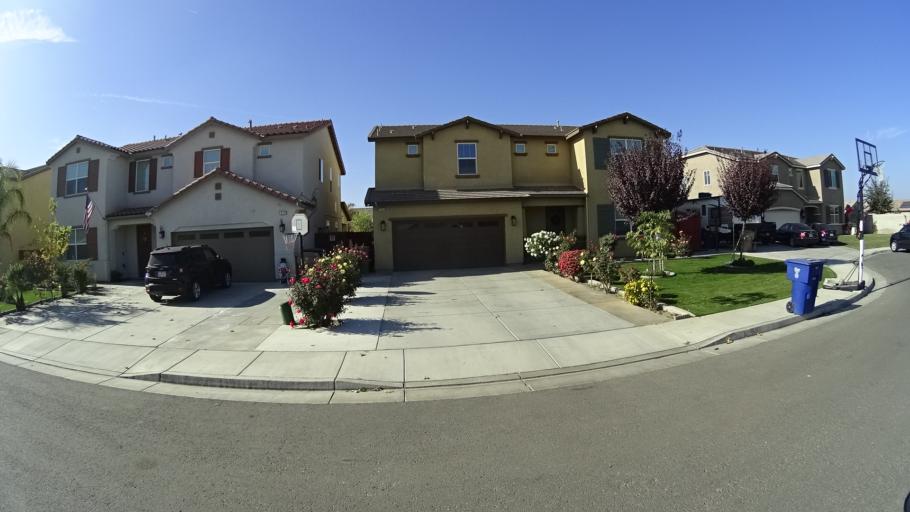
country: US
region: California
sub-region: Kern County
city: Greenfield
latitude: 35.2882
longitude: -119.0609
